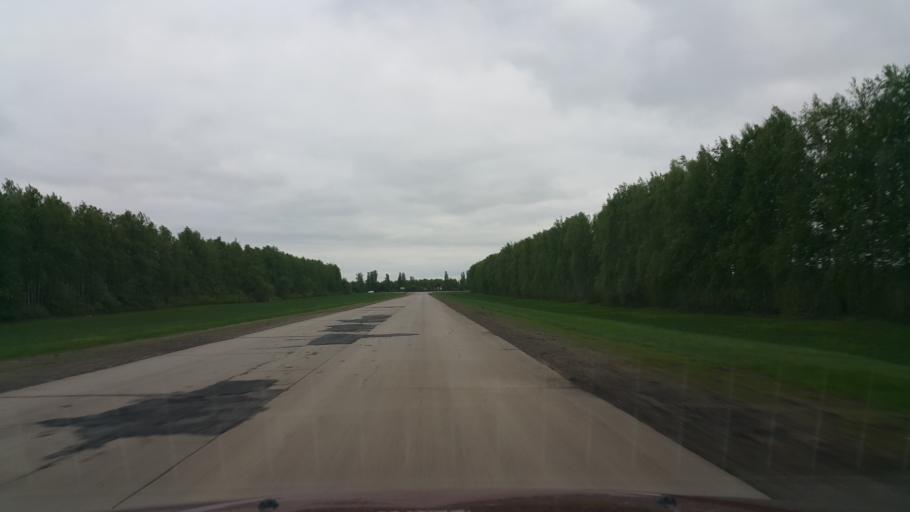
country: RU
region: Tambov
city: Znamenka
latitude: 52.3833
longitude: 41.4199
